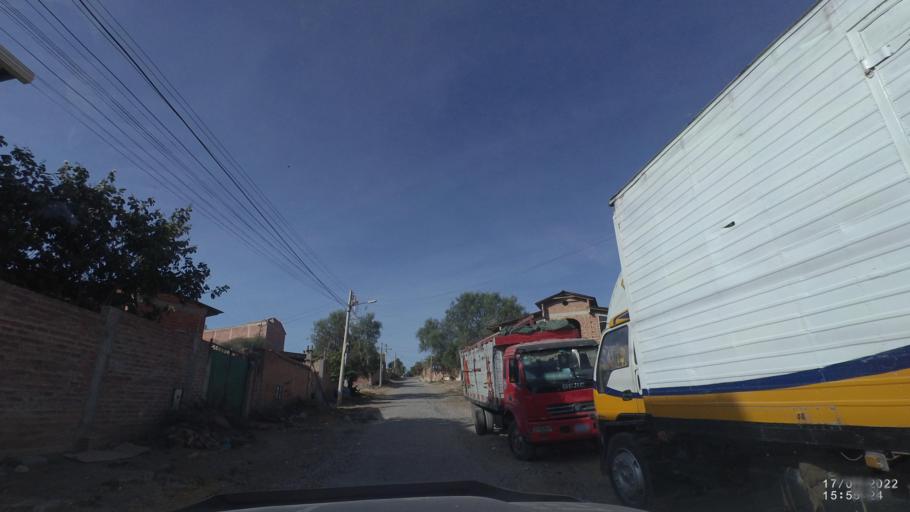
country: BO
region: Cochabamba
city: Sipe Sipe
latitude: -17.4244
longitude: -66.2871
